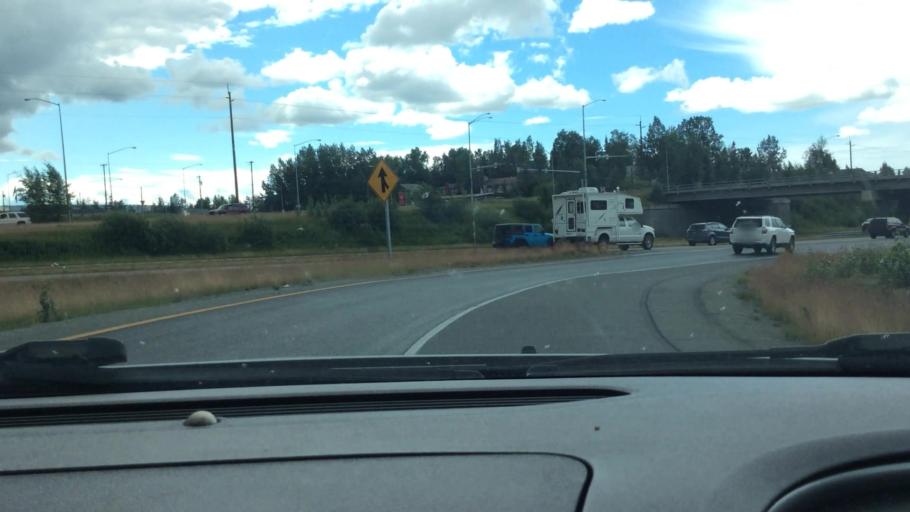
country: US
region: Alaska
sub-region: Anchorage Municipality
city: Anchorage
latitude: 61.2252
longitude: -149.7763
